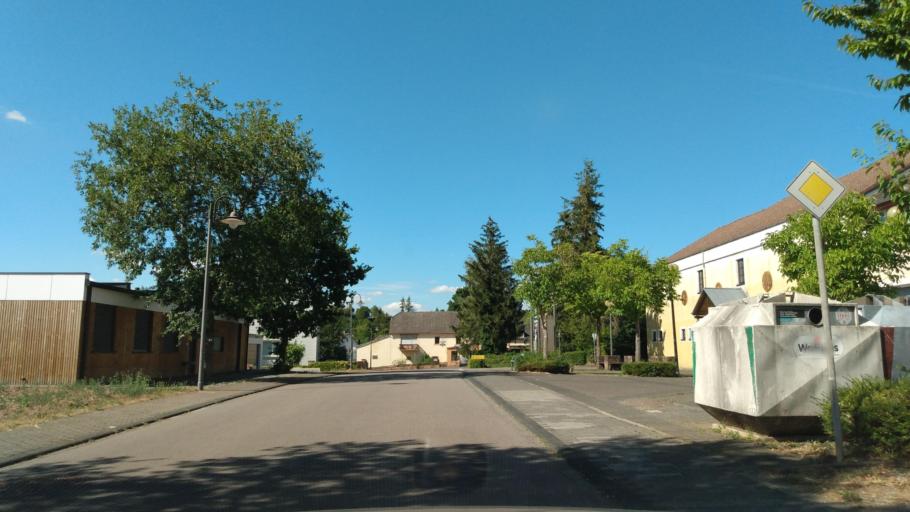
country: DE
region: Rheinland-Pfalz
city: Spangdahlem
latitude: 49.9853
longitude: 6.6802
